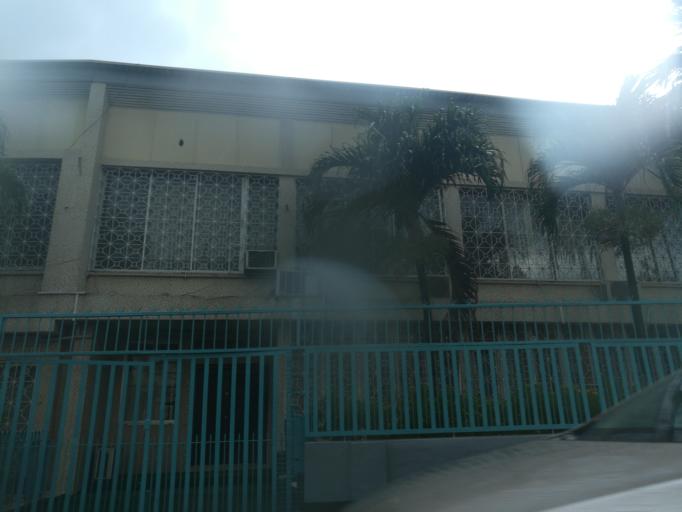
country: NG
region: Lagos
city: Lagos
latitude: 6.4504
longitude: 3.3965
